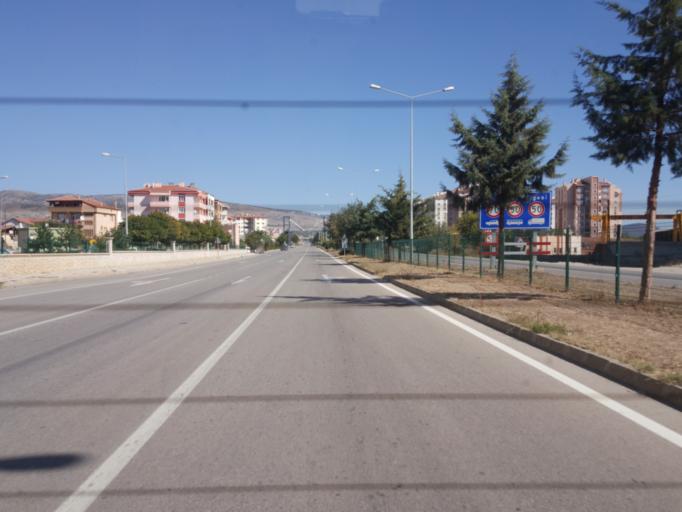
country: TR
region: Tokat
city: Zile
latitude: 40.2977
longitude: 35.8940
